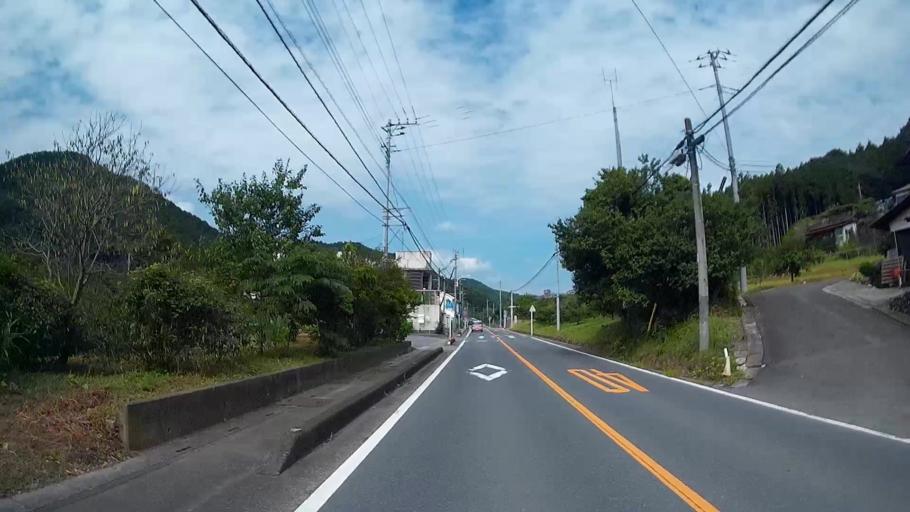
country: JP
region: Saitama
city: Hanno
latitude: 35.8664
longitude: 139.2704
